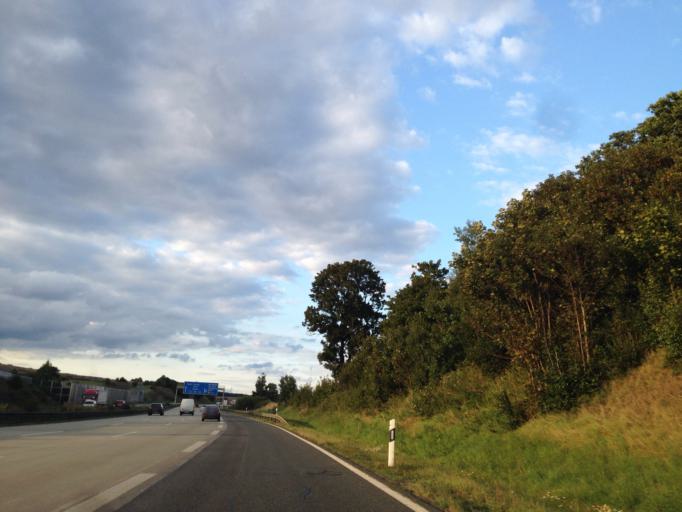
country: DE
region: Thuringia
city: Birkenhugel
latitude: 50.4317
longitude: 11.7987
